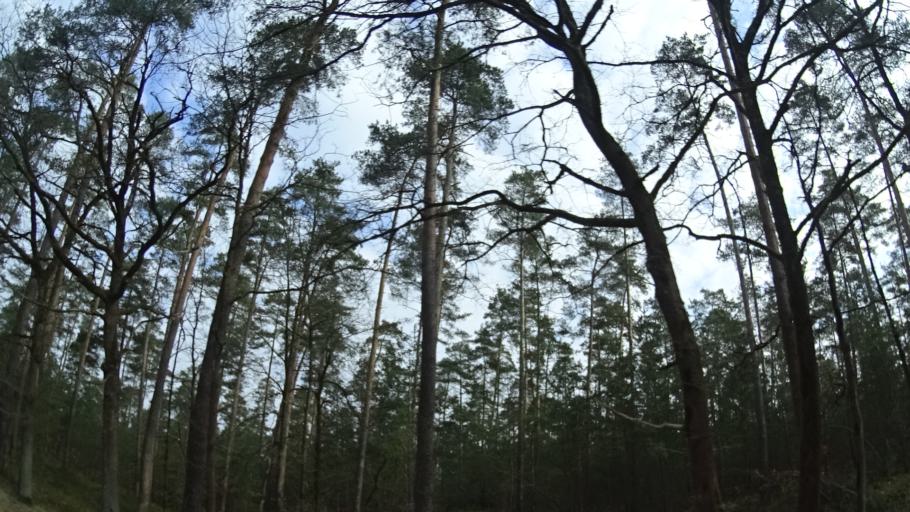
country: DE
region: Bavaria
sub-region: Regierungsbezirk Mittelfranken
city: Winkelhaid
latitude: 49.4051
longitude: 11.3129
